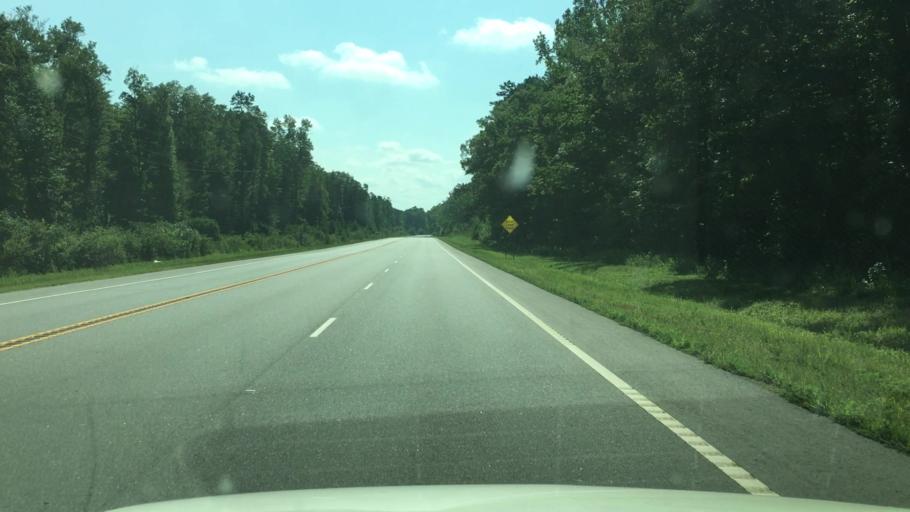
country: US
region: Arkansas
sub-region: Garland County
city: Rockwell
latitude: 34.5181
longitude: -93.3111
